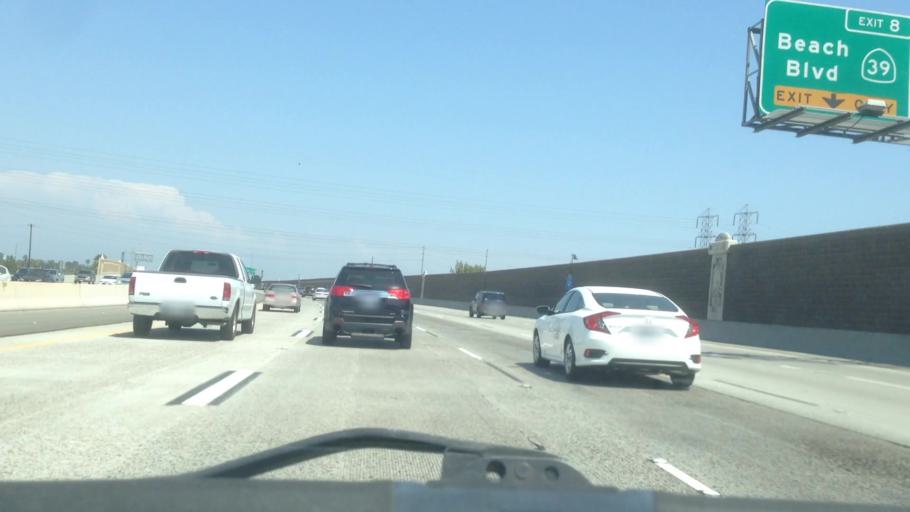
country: US
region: California
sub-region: Orange County
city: Westminster
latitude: 33.7716
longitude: -118.0015
